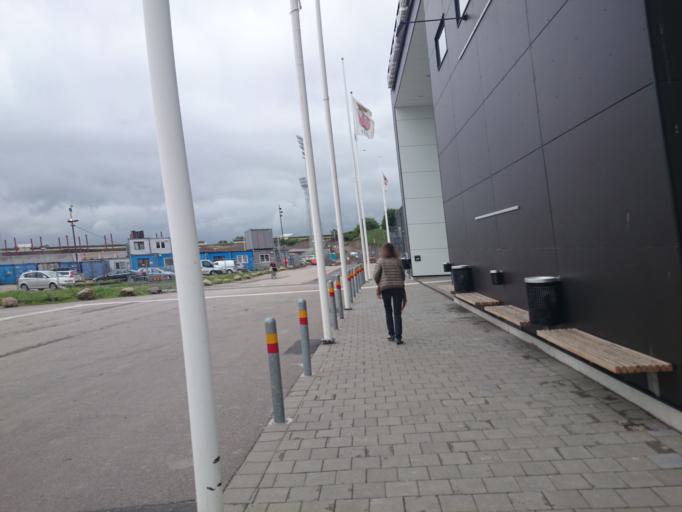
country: SE
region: Skane
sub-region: Lunds Kommun
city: Lund
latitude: 55.6973
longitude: 13.1806
